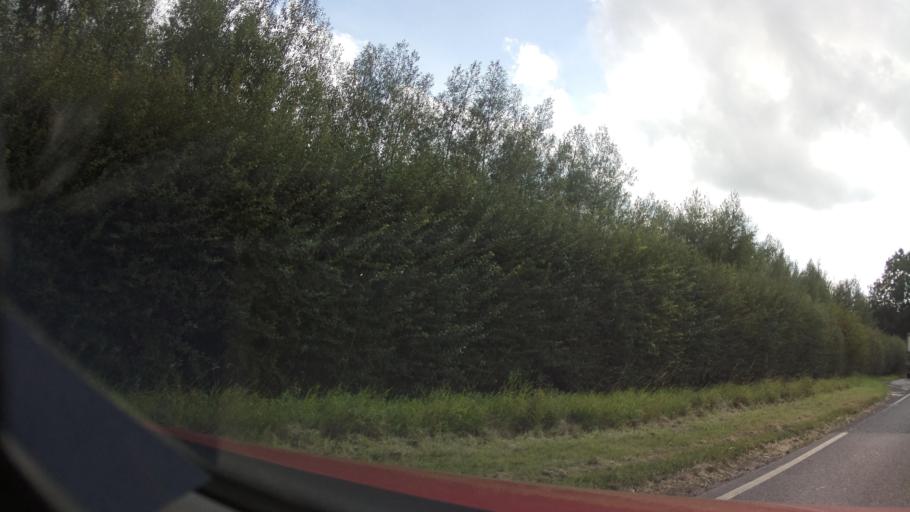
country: GB
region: England
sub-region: Darlington
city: High Coniscliffe
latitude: 54.4657
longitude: -1.6591
